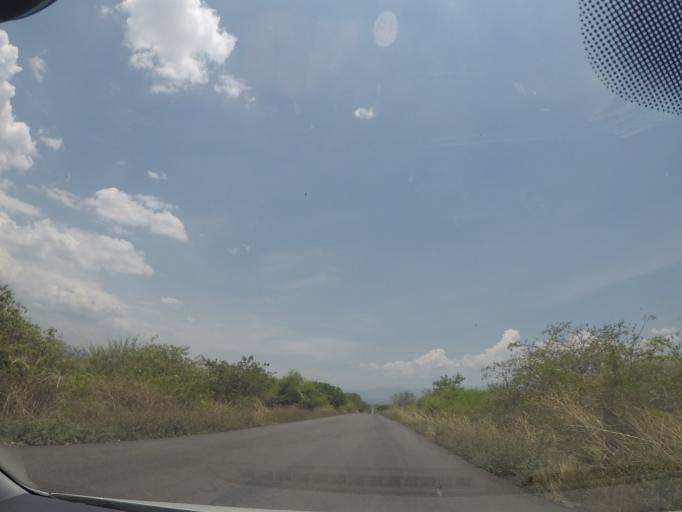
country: MX
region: Oaxaca
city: Santa Maria Jalapa del Marques
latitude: 16.4397
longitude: -95.4737
